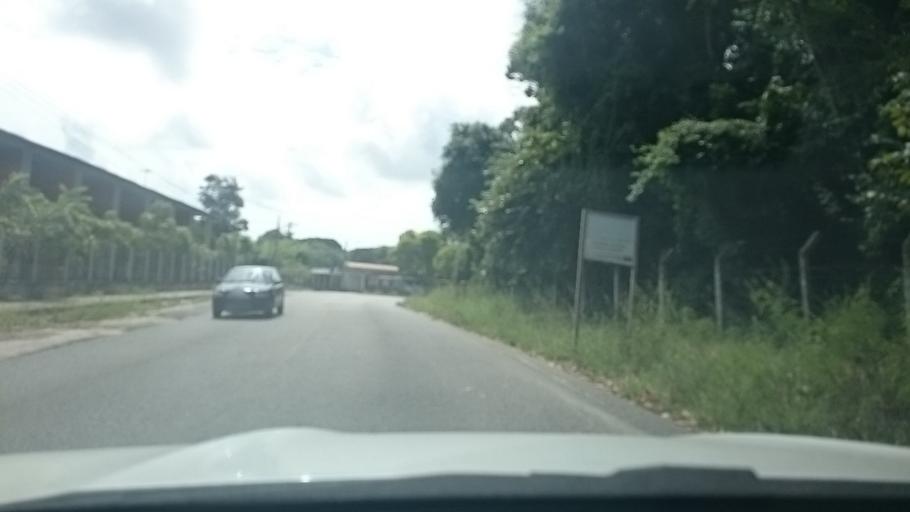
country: BR
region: Paraiba
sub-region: Joao Pessoa
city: Joao Pessoa
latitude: -7.1413
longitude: -34.8457
